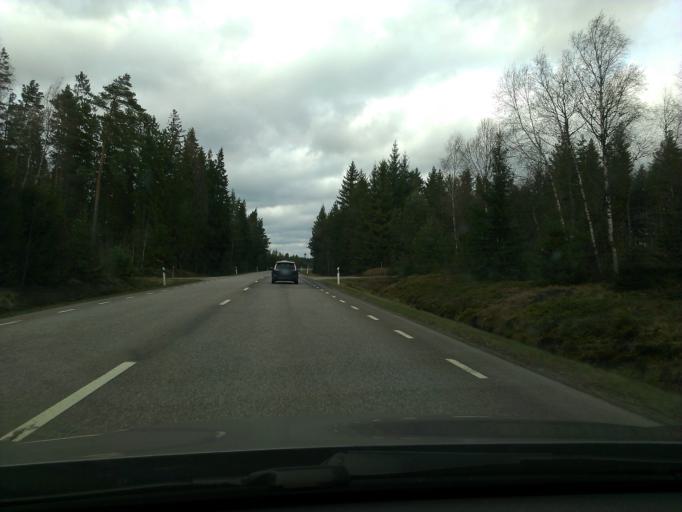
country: SE
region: Kronoberg
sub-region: Almhults Kommun
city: AElmhult
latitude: 56.6171
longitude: 14.2367
